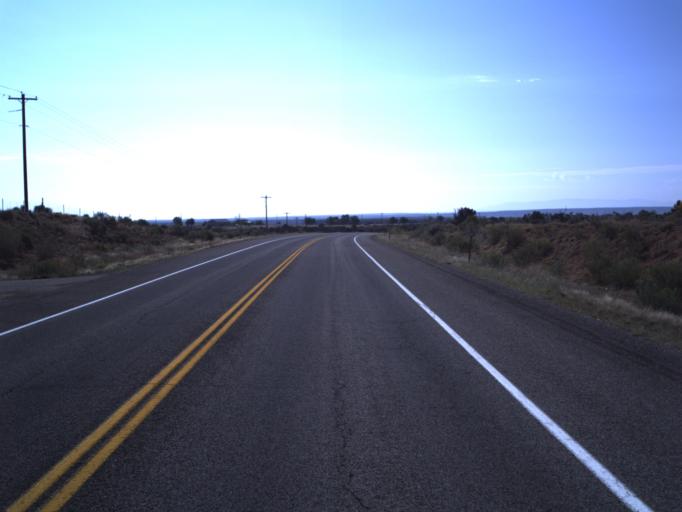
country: US
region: Utah
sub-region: San Juan County
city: Blanding
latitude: 37.4809
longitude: -109.4701
